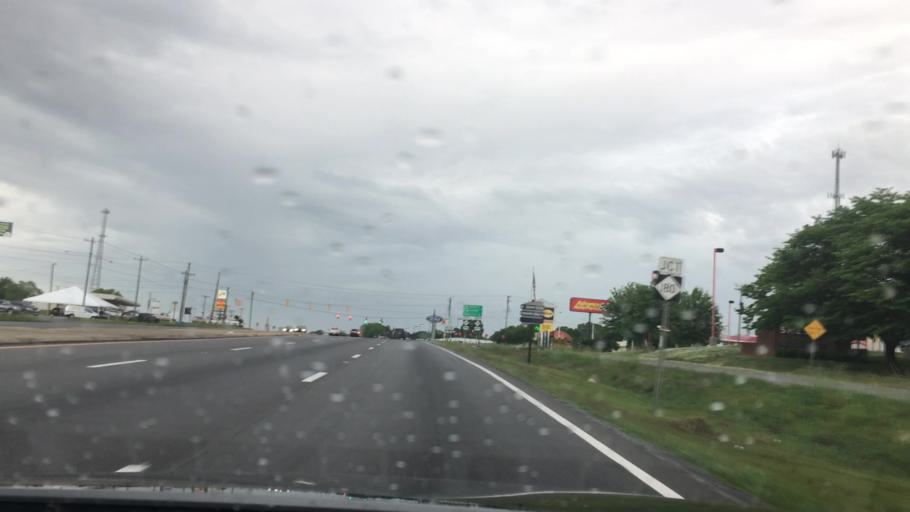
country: US
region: North Carolina
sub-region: Cleveland County
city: Shelby
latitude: 35.2719
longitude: -81.4952
